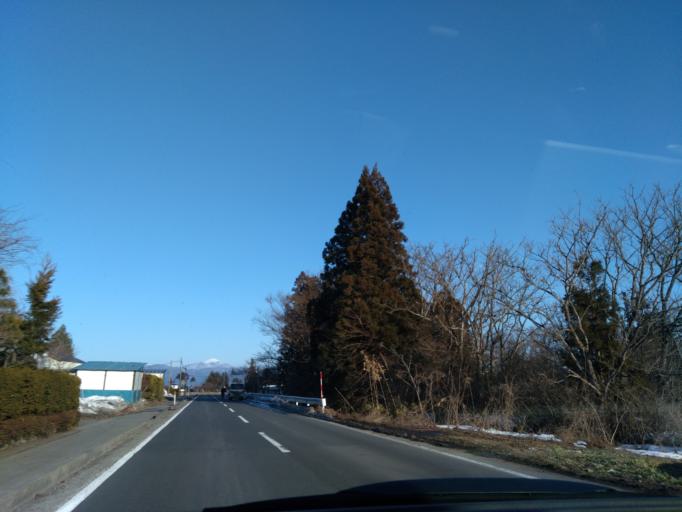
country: JP
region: Iwate
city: Morioka-shi
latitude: 39.5574
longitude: 141.0988
